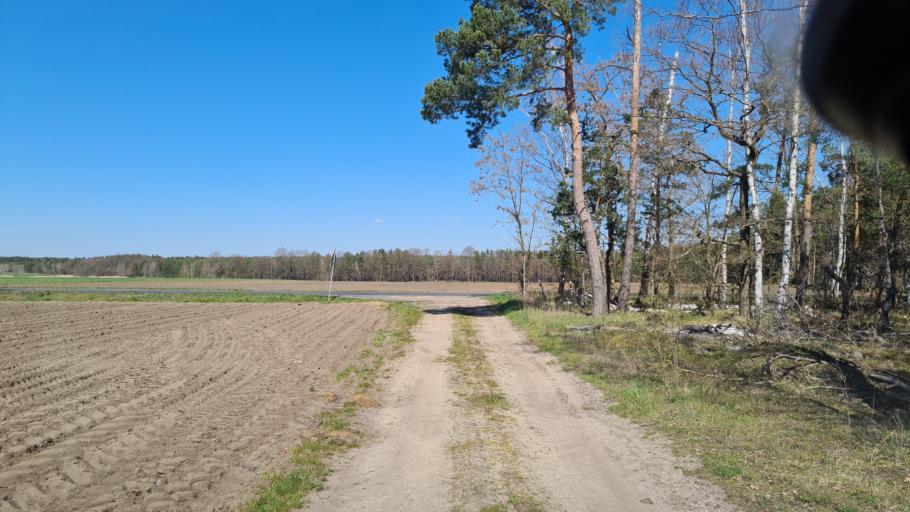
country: DE
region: Brandenburg
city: Ruckersdorf
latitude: 51.5550
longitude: 13.6179
